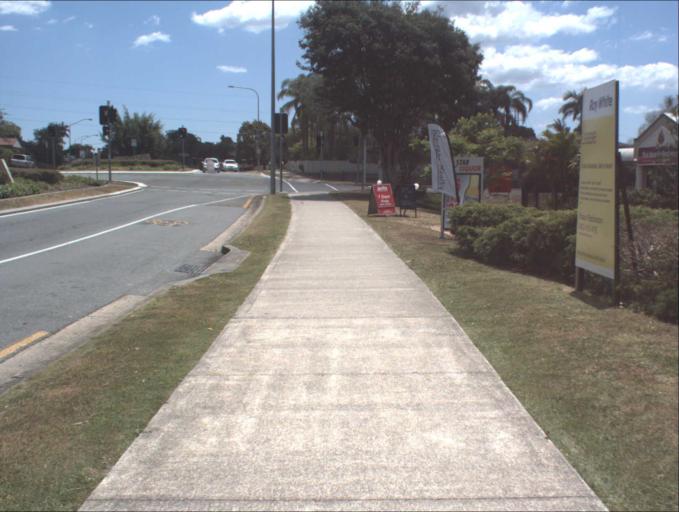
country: AU
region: Queensland
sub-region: Logan
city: Windaroo
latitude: -27.7289
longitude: 153.2081
